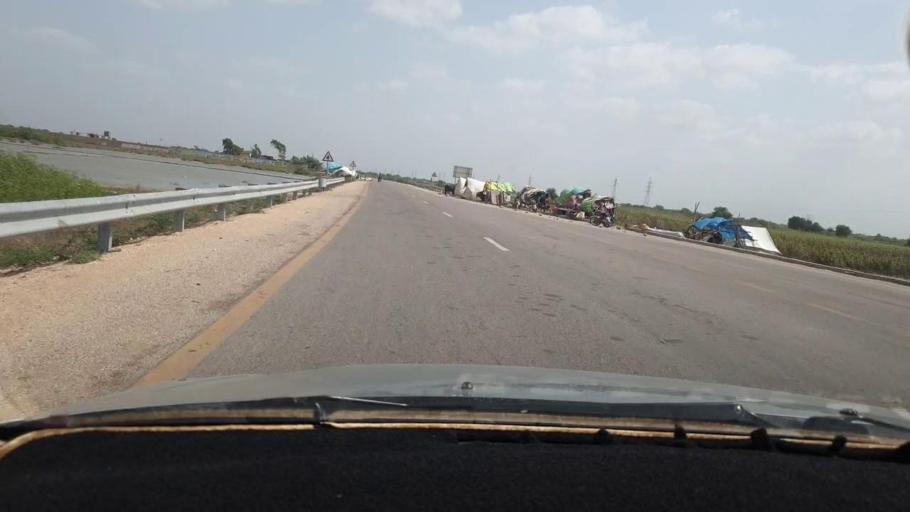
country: PK
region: Sindh
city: Digri
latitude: 25.0515
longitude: 69.2229
